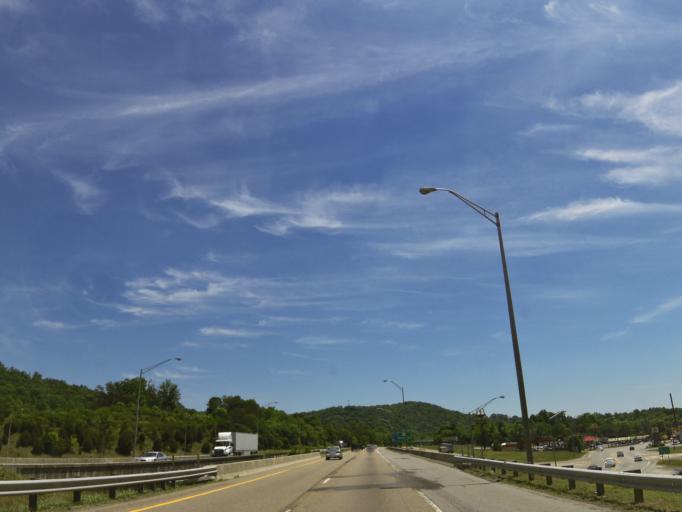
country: US
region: Tennessee
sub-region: Anderson County
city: Rocky Top
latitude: 36.2338
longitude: -84.1612
